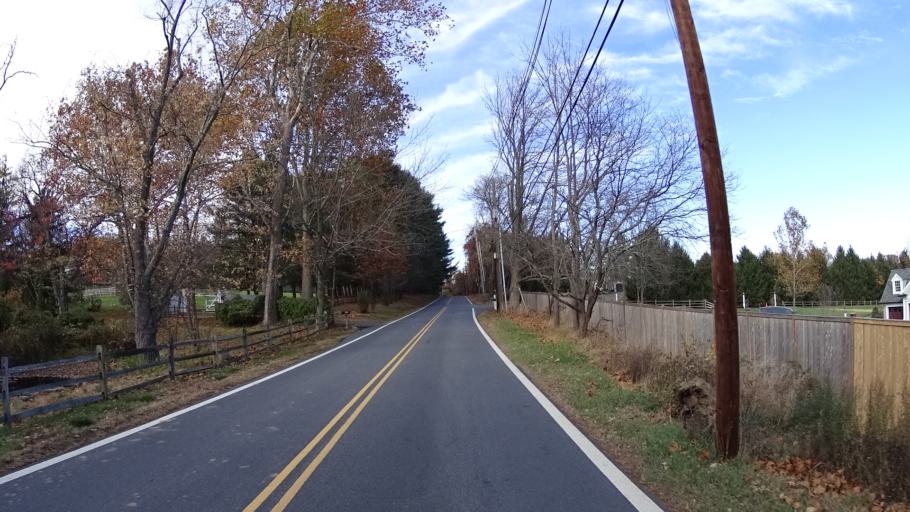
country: US
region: New Jersey
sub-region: Morris County
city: Madison
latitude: 40.7615
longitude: -74.4566
